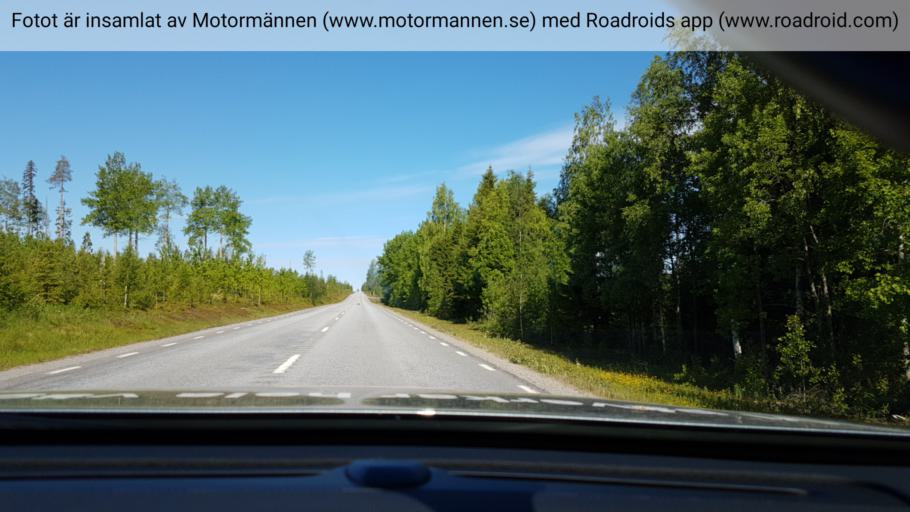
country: SE
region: Vaesterbotten
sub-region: Bjurholms Kommun
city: Bjurholm
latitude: 63.9482
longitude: 18.9031
